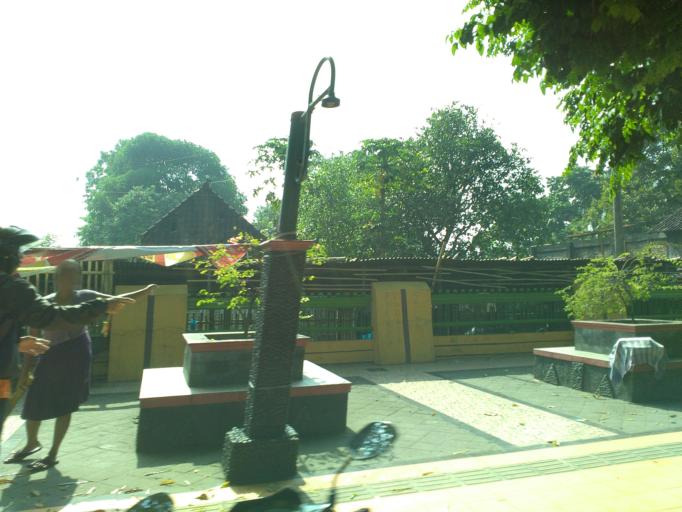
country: ID
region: Central Java
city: Delanggu
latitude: -7.6234
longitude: 110.6976
